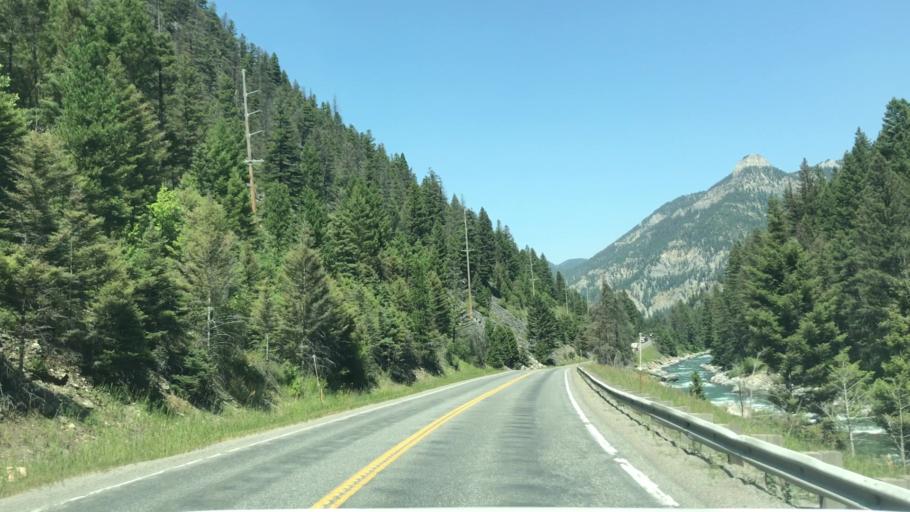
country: US
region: Montana
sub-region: Gallatin County
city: Big Sky
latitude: 45.4225
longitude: -111.2342
